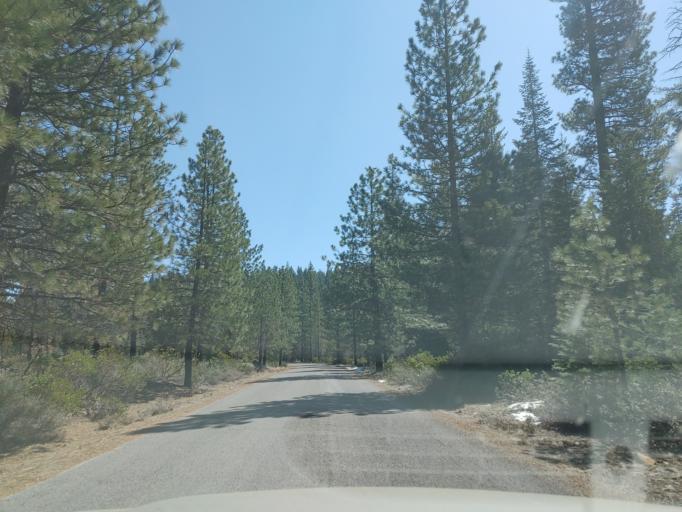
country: US
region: California
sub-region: Siskiyou County
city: McCloud
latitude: 41.2488
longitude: -121.9562
